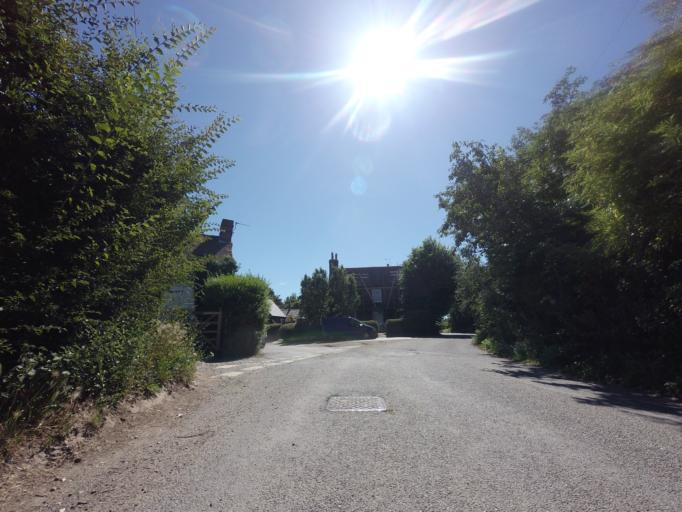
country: GB
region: England
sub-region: Kent
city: Ash
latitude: 51.3033
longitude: 1.2348
